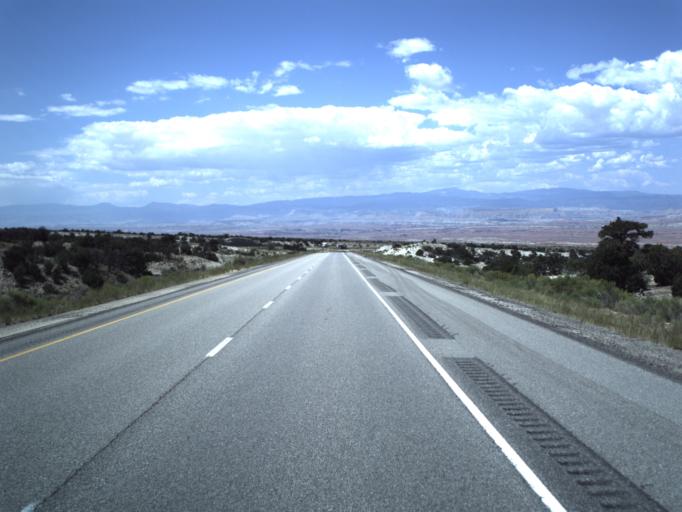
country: US
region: Utah
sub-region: Emery County
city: Ferron
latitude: 38.8450
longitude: -110.9472
